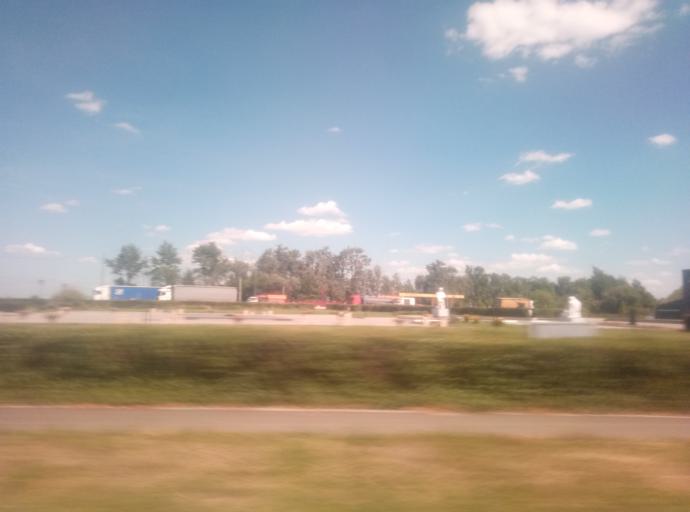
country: RU
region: Tula
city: Kireyevsk
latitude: 54.0195
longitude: 37.9077
